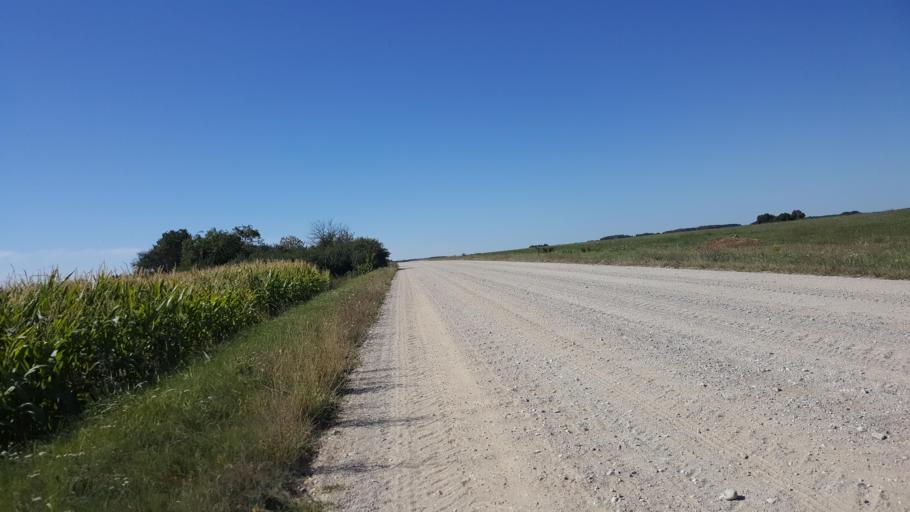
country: PL
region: Lublin Voivodeship
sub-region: Powiat bialski
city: Rokitno
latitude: 52.2274
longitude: 23.3301
